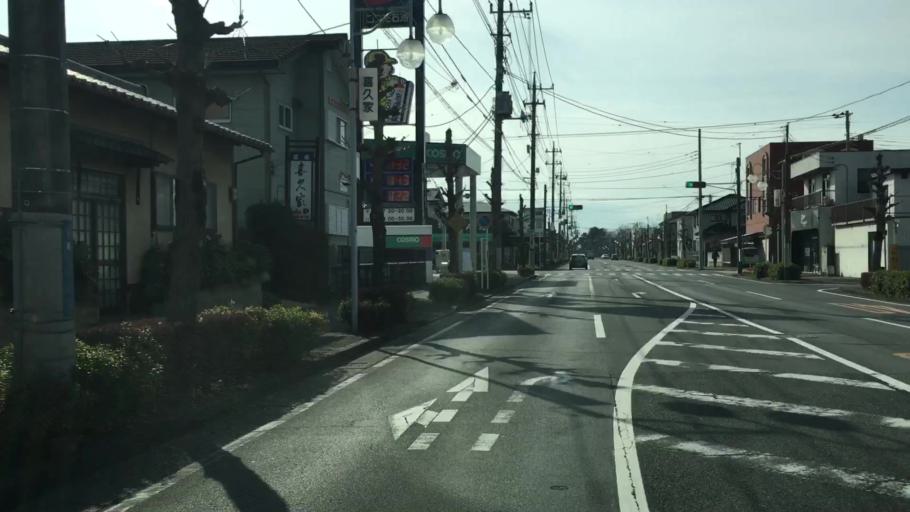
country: JP
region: Saitama
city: Menuma
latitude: 36.2499
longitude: 139.4111
